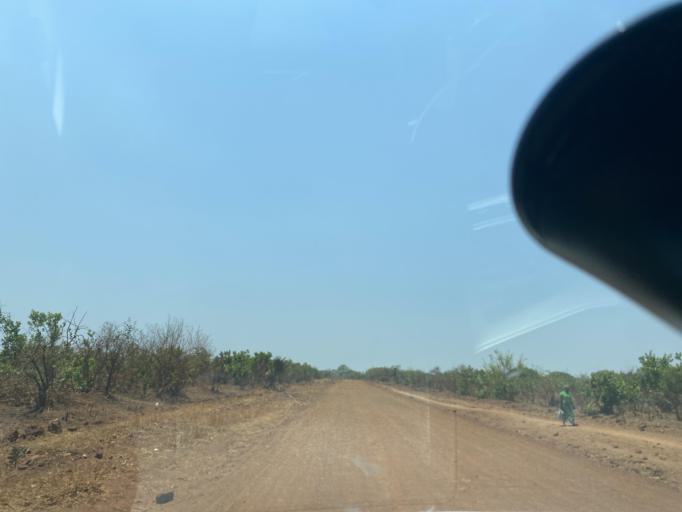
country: ZM
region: Lusaka
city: Lusaka
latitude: -15.4543
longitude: 27.9451
